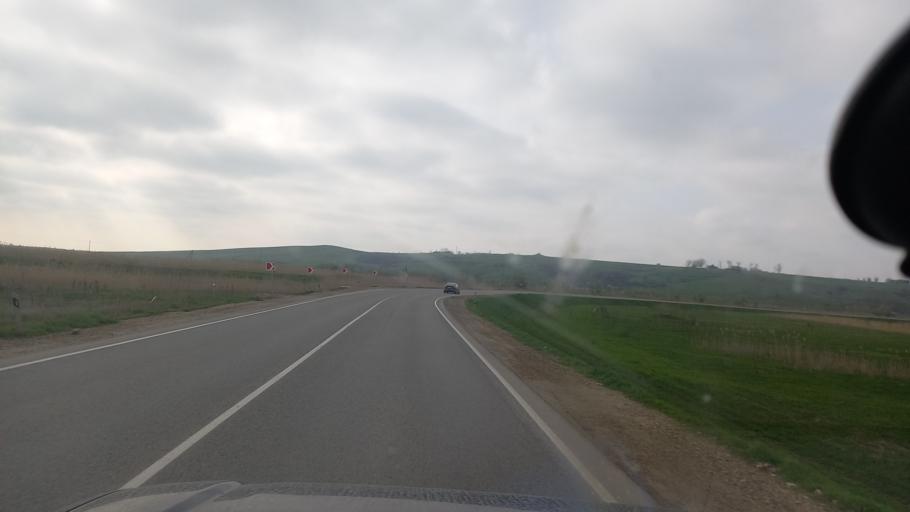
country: RU
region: Krasnodarskiy
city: Varenikovskaya
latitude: 45.1742
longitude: 37.6547
